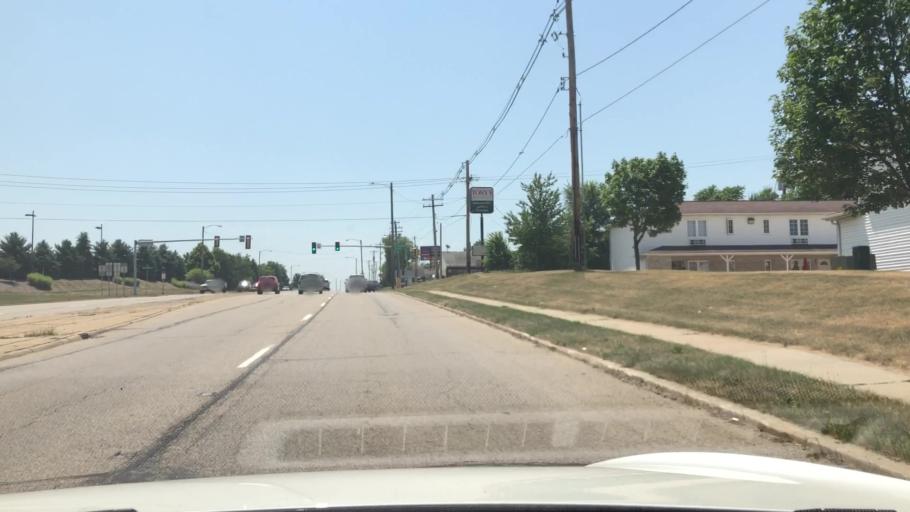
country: US
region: Illinois
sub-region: McLean County
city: Bloomington
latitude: 40.4577
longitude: -88.9930
